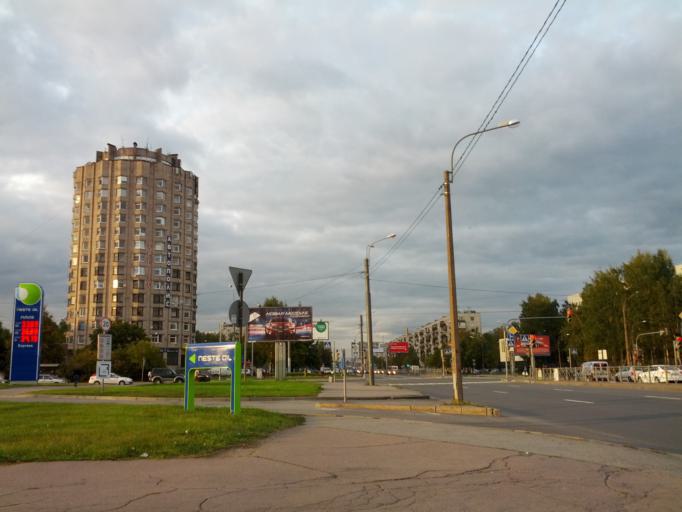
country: RU
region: St.-Petersburg
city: Krasnogvargeisky
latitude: 59.9524
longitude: 30.4366
